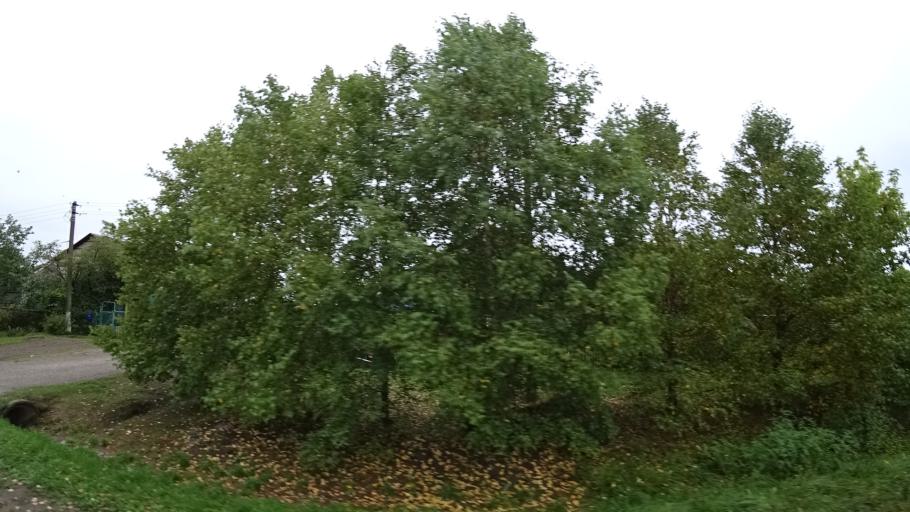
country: RU
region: Primorskiy
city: Monastyrishche
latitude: 44.2327
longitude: 132.4619
